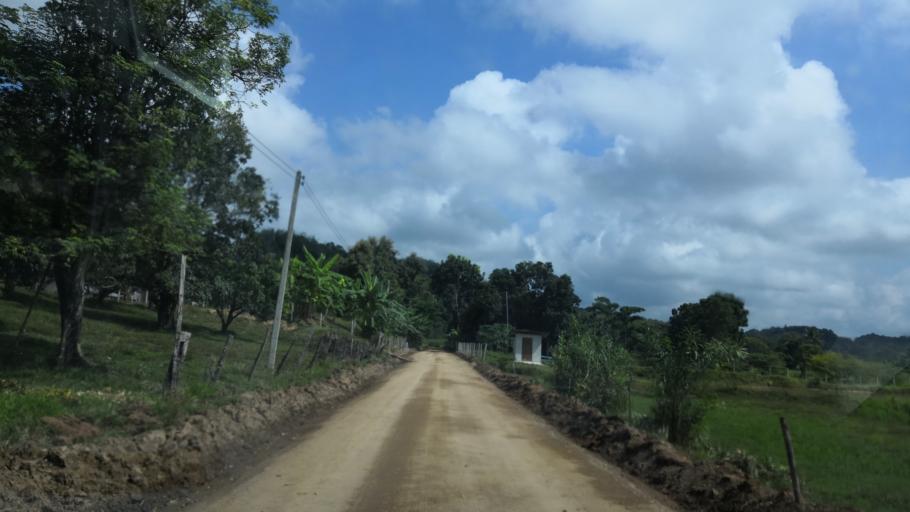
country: TH
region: Chiang Rai
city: Wiang Chiang Rung
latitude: 20.0303
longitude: 100.0524
